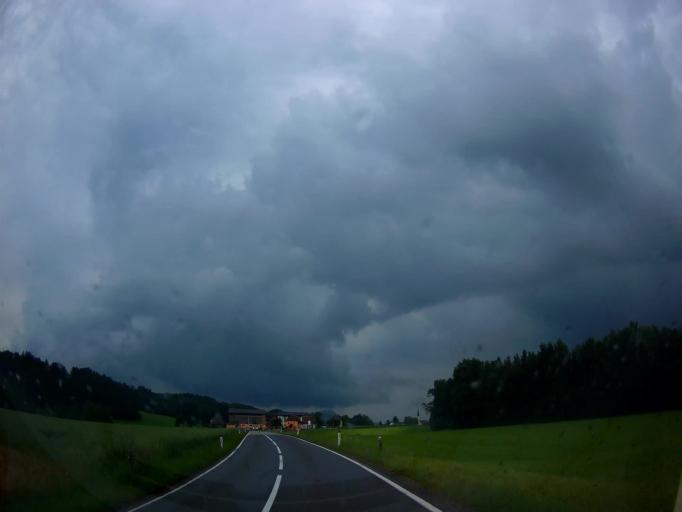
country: AT
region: Salzburg
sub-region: Politischer Bezirk Salzburg-Umgebung
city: Mattsee
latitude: 48.0234
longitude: 13.1328
